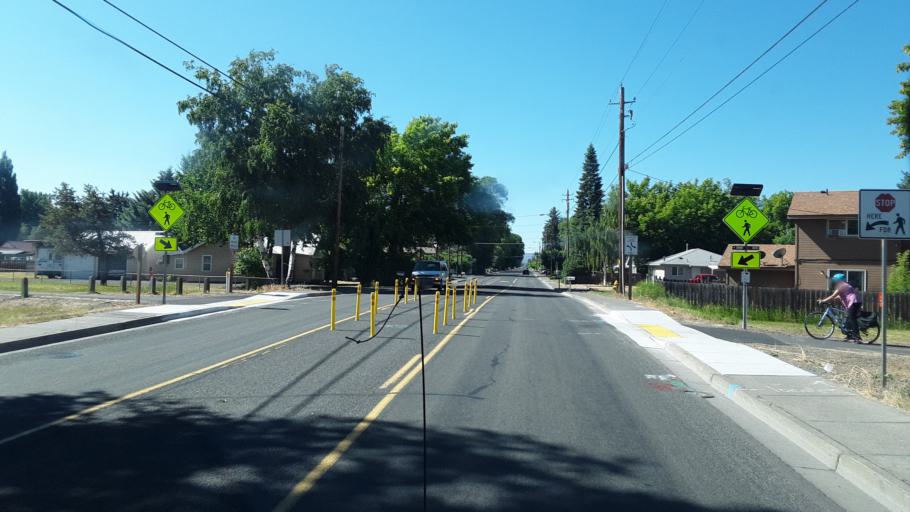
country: US
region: Oregon
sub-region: Klamath County
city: Altamont
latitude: 42.1984
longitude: -121.7228
